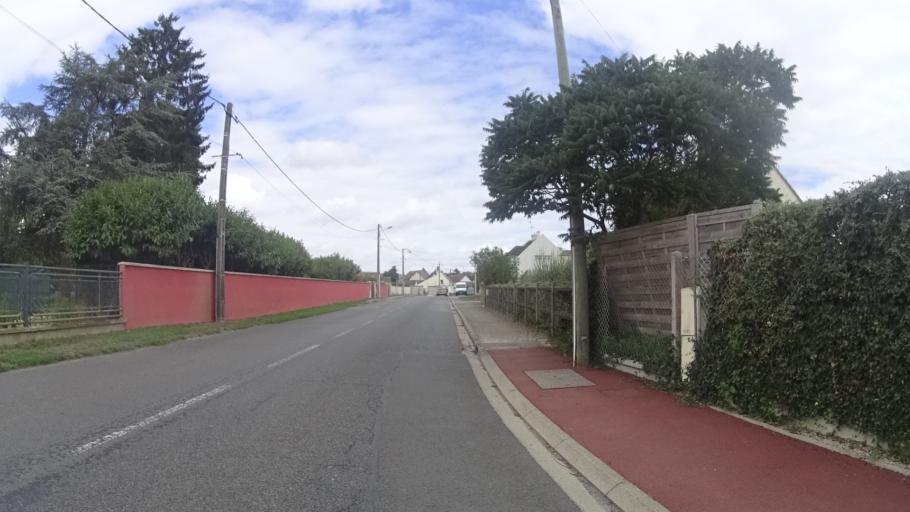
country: FR
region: Picardie
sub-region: Departement de l'Oise
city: Noyon
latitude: 49.5564
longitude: 2.9918
